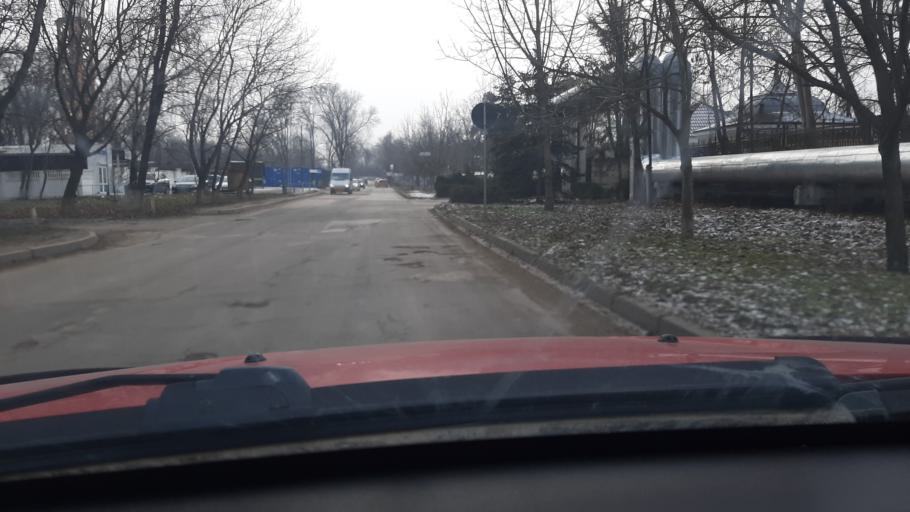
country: MD
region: Chisinau
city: Chisinau
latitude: 46.9752
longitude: 28.8942
